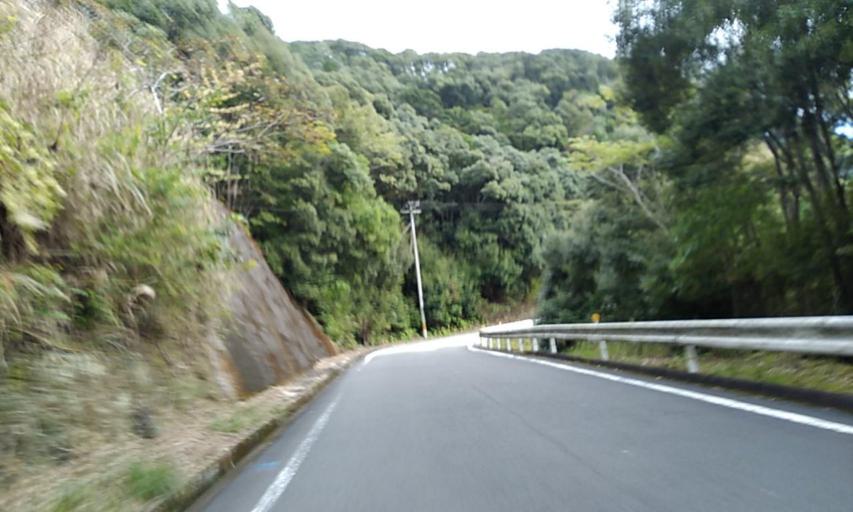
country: JP
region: Wakayama
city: Shingu
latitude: 33.5432
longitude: 135.8345
